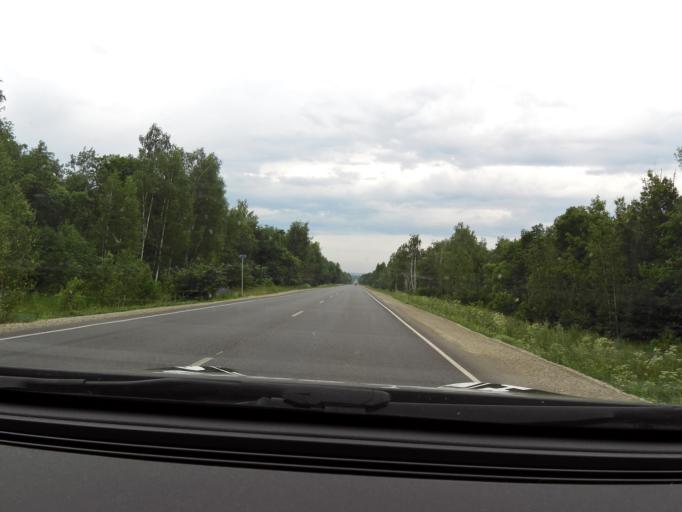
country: RU
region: Bashkortostan
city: Ulu-Telyak
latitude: 54.8379
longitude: 57.0273
